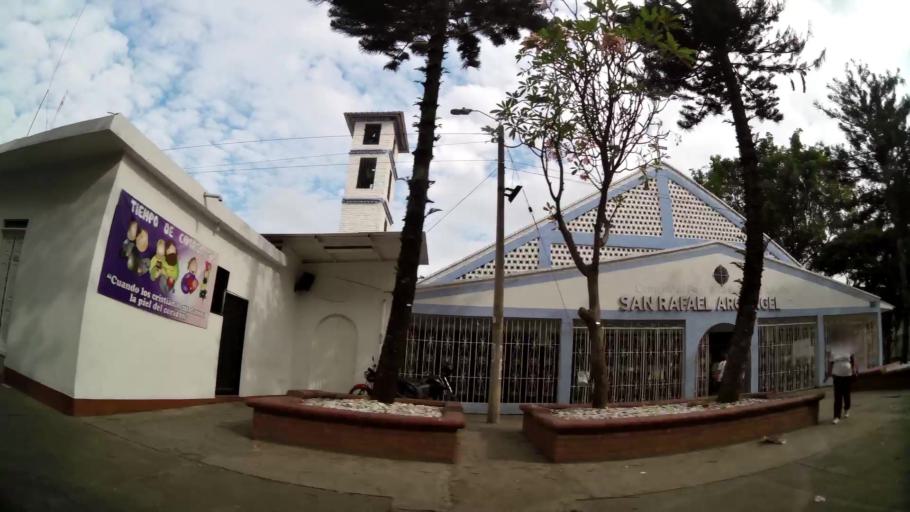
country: CO
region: Valle del Cauca
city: Cali
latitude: 3.4741
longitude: -76.4899
